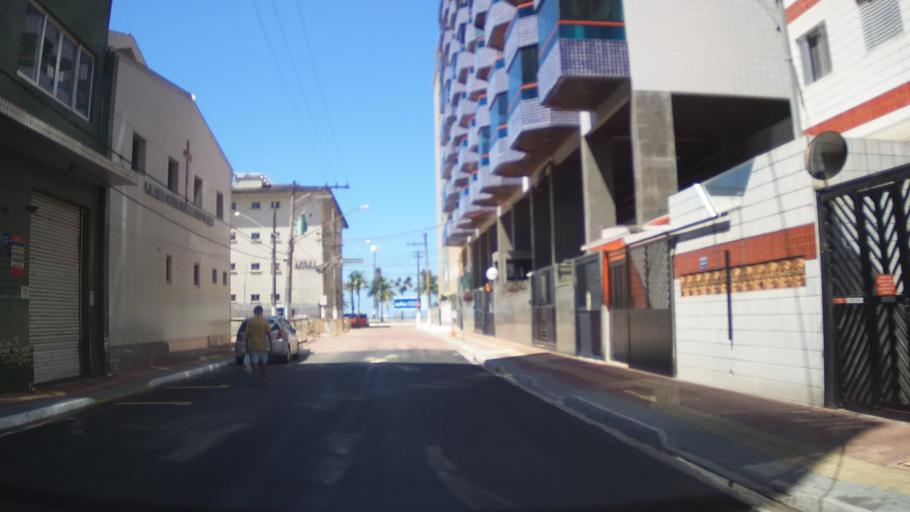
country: BR
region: Sao Paulo
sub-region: Praia Grande
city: Praia Grande
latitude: -24.0290
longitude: -46.4755
